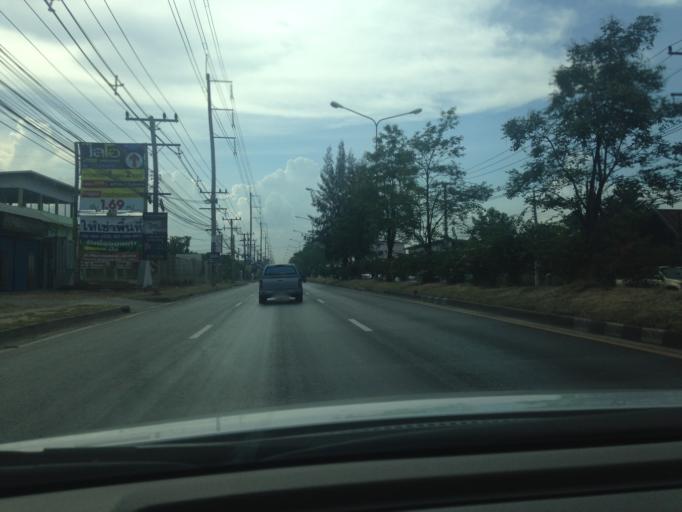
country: TH
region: Pathum Thani
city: Khlong Luang
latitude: 14.0661
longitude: 100.6713
